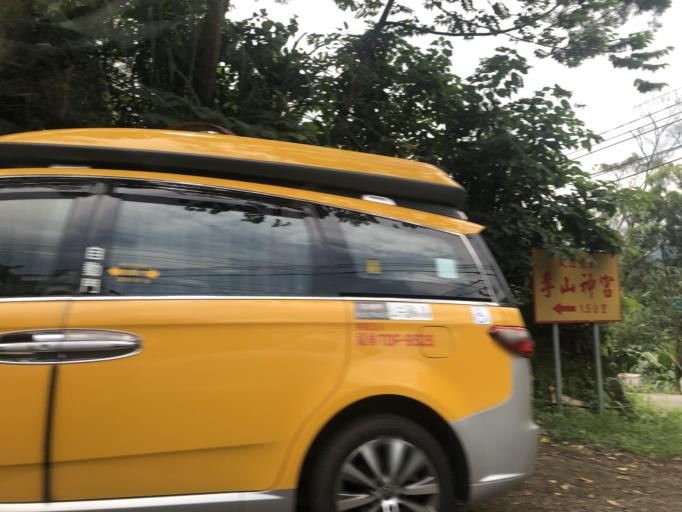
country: TW
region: Taiwan
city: Daxi
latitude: 24.8758
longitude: 121.4164
